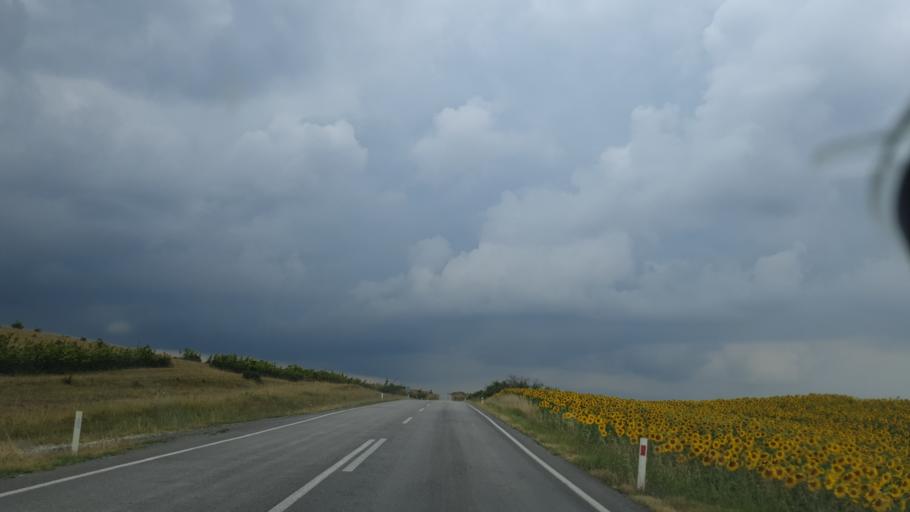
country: TR
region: Tekirdag
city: Hayrabolu
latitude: 41.2217
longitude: 27.0194
